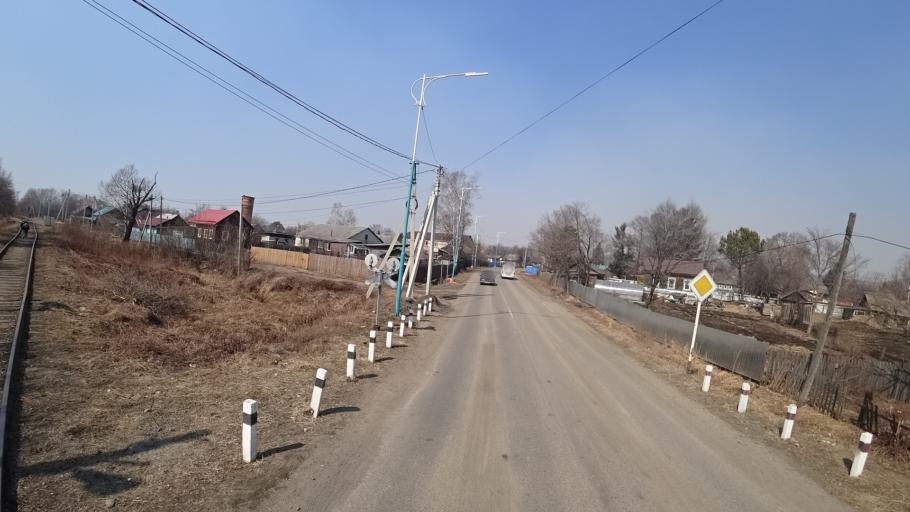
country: RU
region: Amur
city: Novobureyskiy
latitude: 49.7943
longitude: 129.8921
